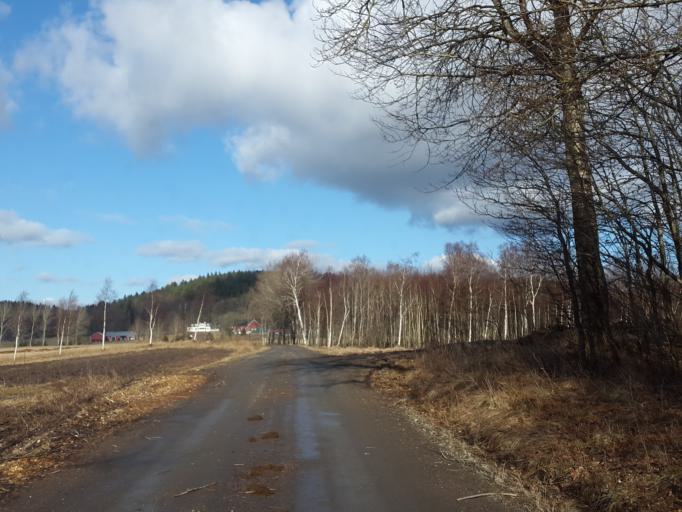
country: SE
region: Vaestra Goetaland
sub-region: Lerums Kommun
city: Olstorp
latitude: 57.8292
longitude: 12.2209
